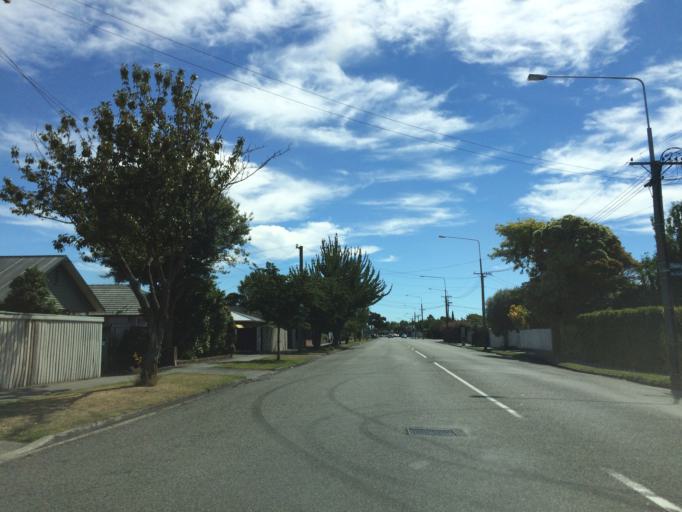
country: NZ
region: Canterbury
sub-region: Christchurch City
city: Christchurch
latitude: -43.5016
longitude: 172.5843
